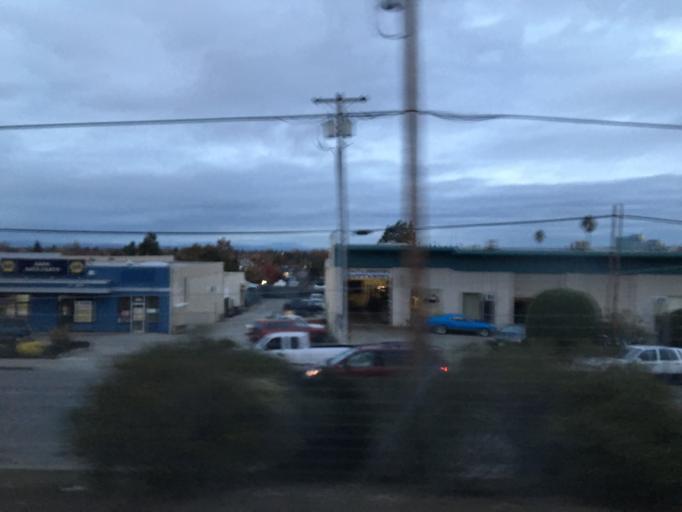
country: US
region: California
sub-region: San Mateo County
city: Belmont
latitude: 37.5258
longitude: -122.2816
